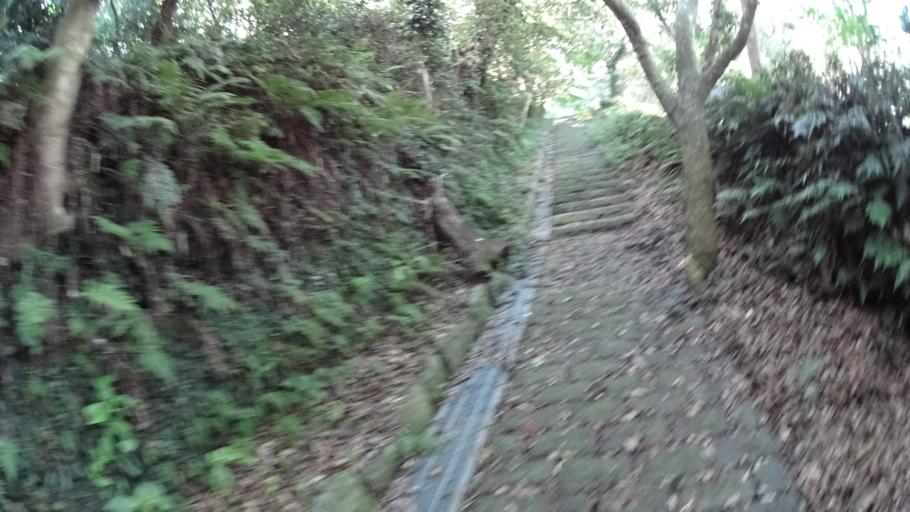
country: JP
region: Shizuoka
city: Shimoda
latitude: 34.5269
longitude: 139.2771
